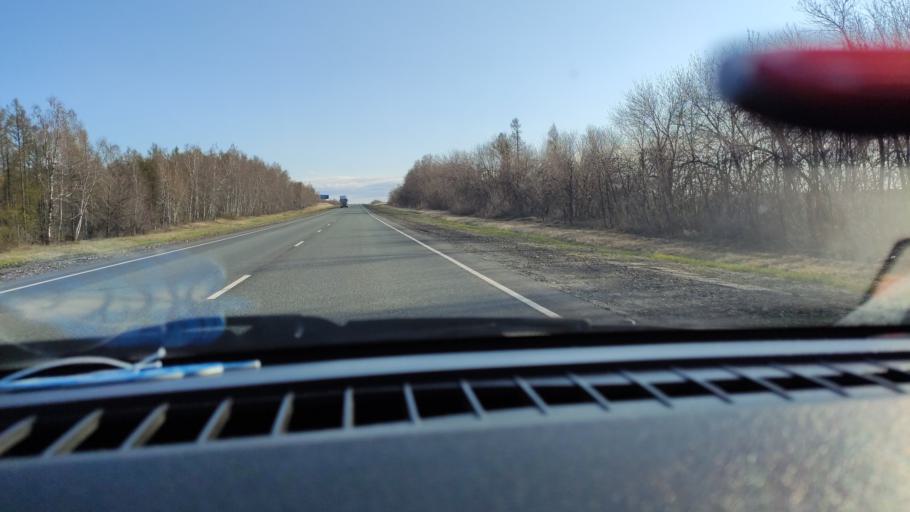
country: RU
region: Saratov
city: Khvalynsk
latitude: 52.5840
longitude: 48.1210
